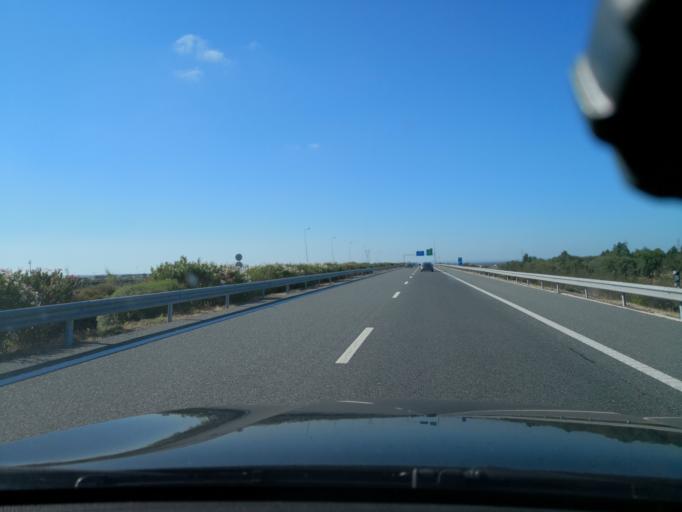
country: PT
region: Beja
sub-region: Ourique
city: Ourique
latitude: 37.6713
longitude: -8.1597
